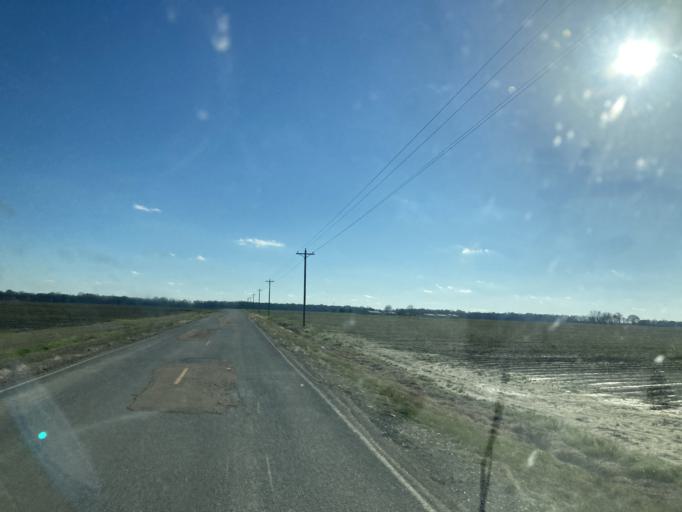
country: US
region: Mississippi
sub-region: Yazoo County
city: Yazoo City
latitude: 32.9306
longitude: -90.5058
